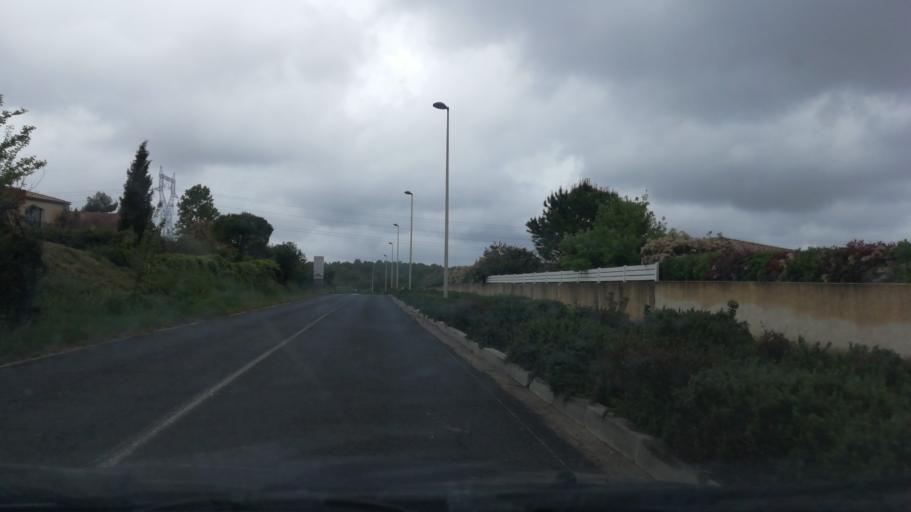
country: FR
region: Languedoc-Roussillon
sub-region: Departement de l'Herault
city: Saint-Gely-du-Fesc
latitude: 43.7027
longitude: 3.8034
